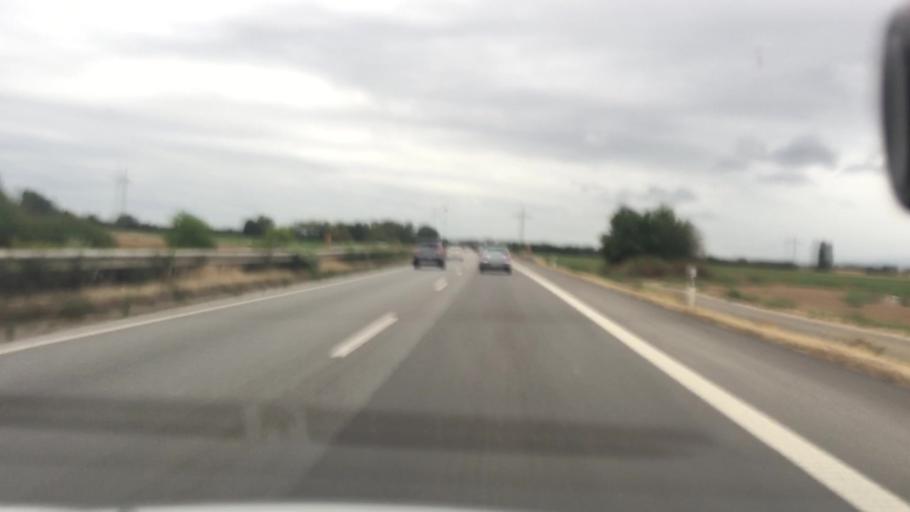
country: DE
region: Rheinland-Pfalz
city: Hochdorf-Assenheim
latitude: 49.4065
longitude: 8.2803
